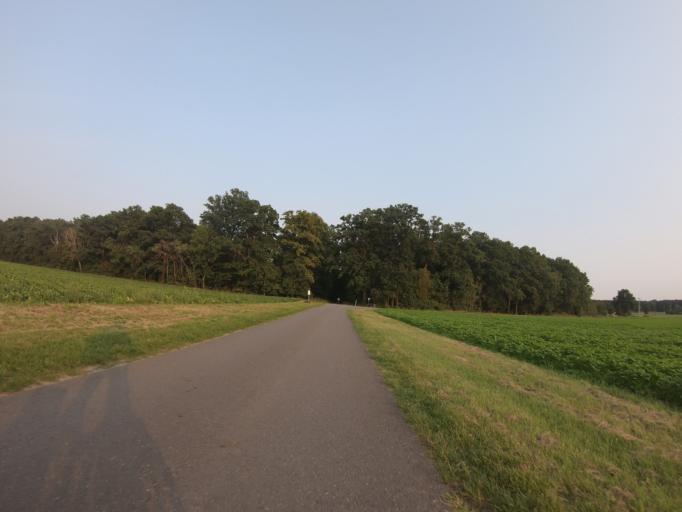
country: DE
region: Lower Saxony
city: Leiferde
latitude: 52.4347
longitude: 10.4478
